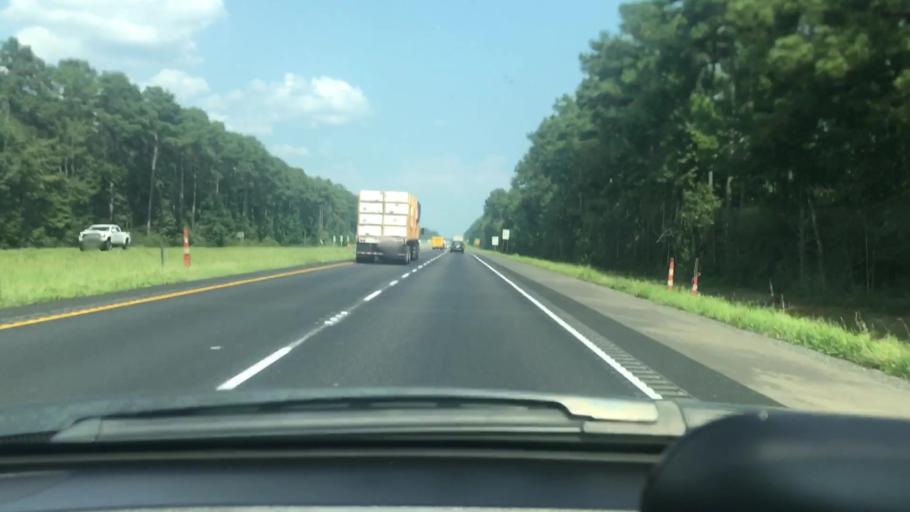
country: US
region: Louisiana
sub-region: Livingston Parish
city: Albany
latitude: 30.4745
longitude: -90.6598
